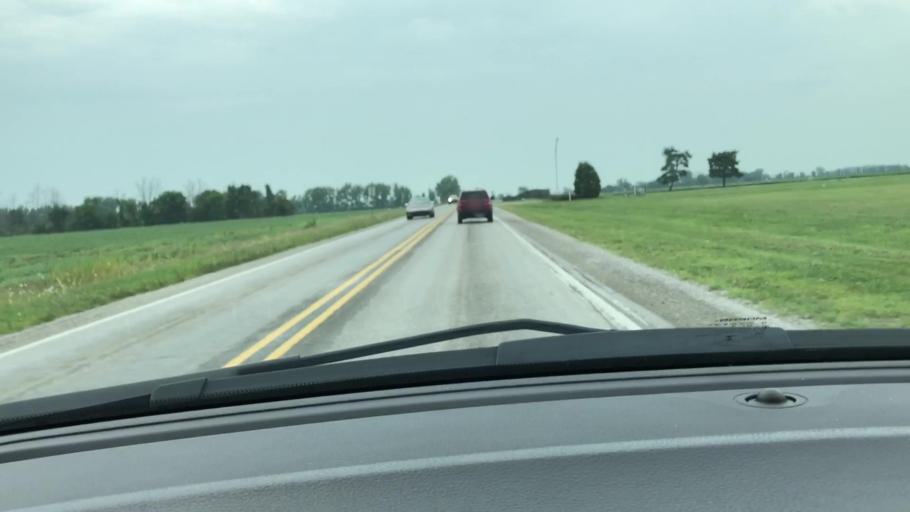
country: US
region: Michigan
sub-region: Saginaw County
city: Freeland
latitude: 43.5329
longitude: -84.0952
